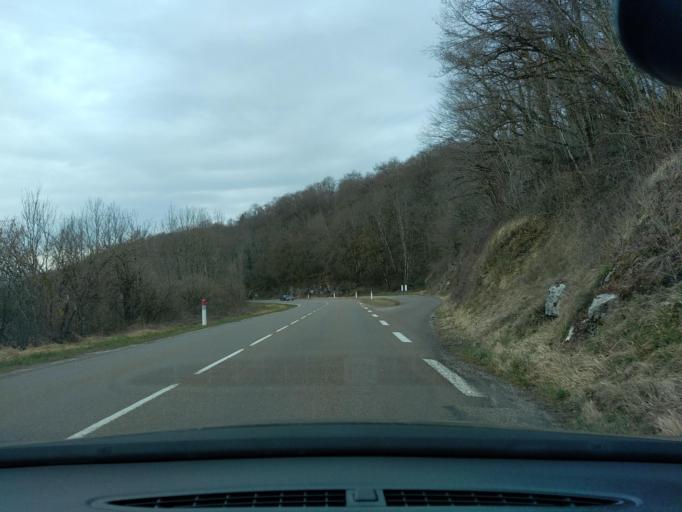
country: FR
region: Franche-Comte
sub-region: Departement du Jura
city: Orgelet
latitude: 46.4918
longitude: 5.5850
